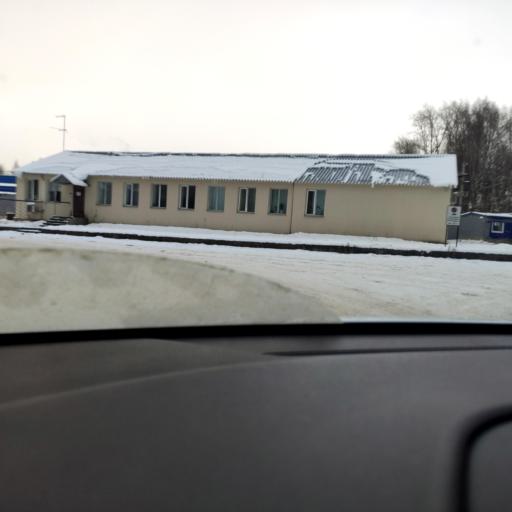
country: RU
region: Tatarstan
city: Osinovo
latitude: 55.8890
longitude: 48.8286
